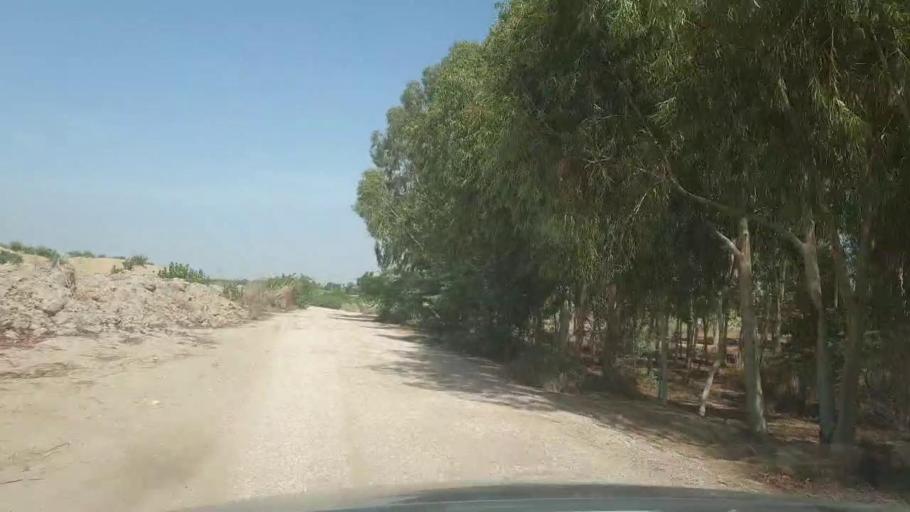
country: PK
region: Sindh
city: Khairpur
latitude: 27.3958
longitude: 69.0722
